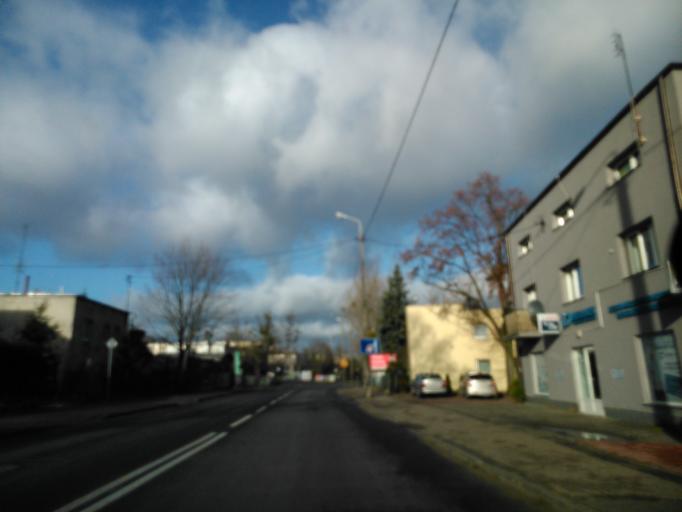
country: PL
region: Kujawsko-Pomorskie
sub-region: Torun
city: Torun
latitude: 52.9977
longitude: 18.6232
